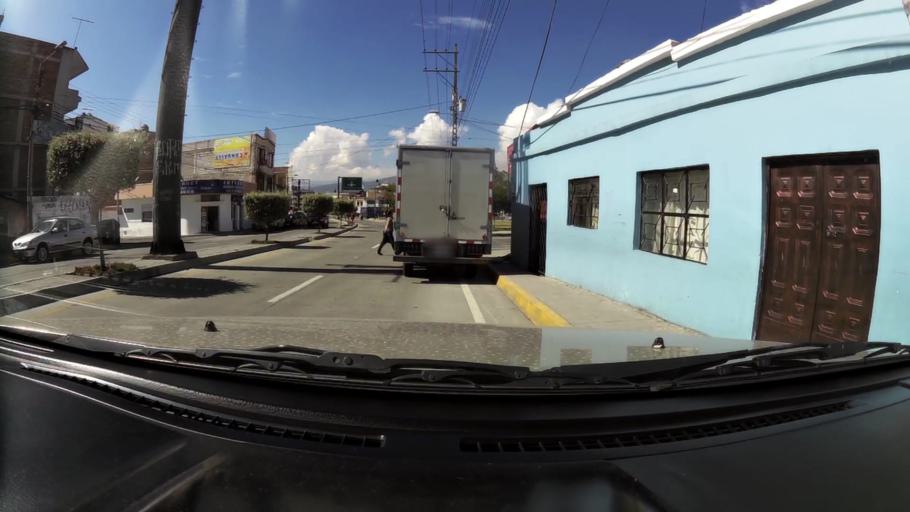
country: EC
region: Chimborazo
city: Riobamba
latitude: -1.6624
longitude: -78.6491
